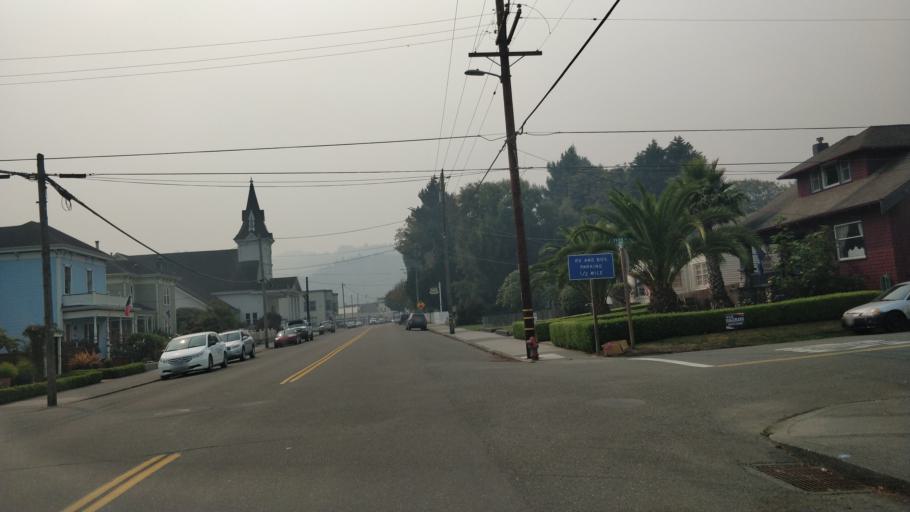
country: US
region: California
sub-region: Humboldt County
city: Ferndale
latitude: 40.5797
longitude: -124.2609
